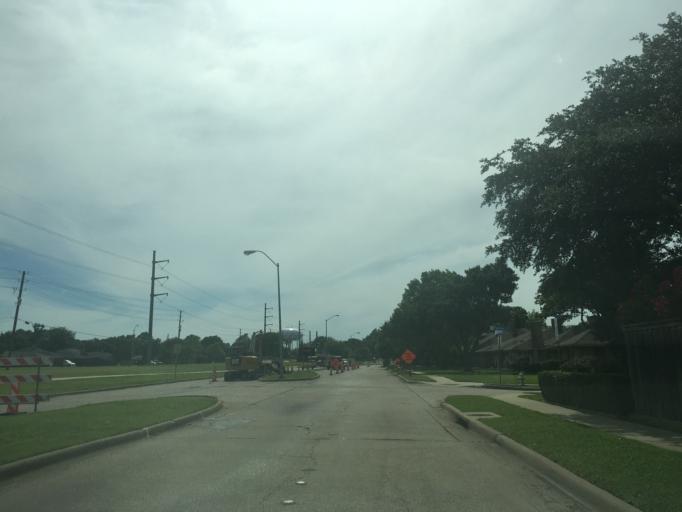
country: US
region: Texas
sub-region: Dallas County
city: Richardson
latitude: 32.9387
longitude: -96.7067
